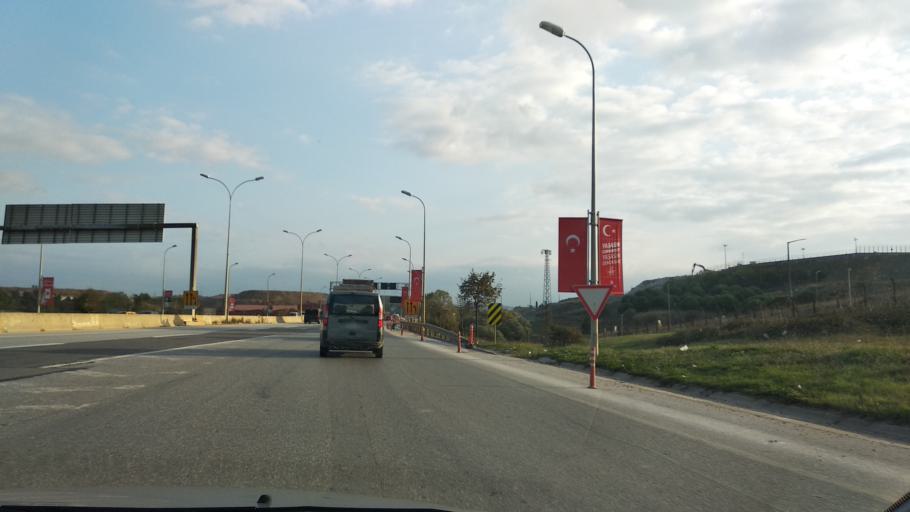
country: TR
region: Istanbul
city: Pendik
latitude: 40.9112
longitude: 29.3262
